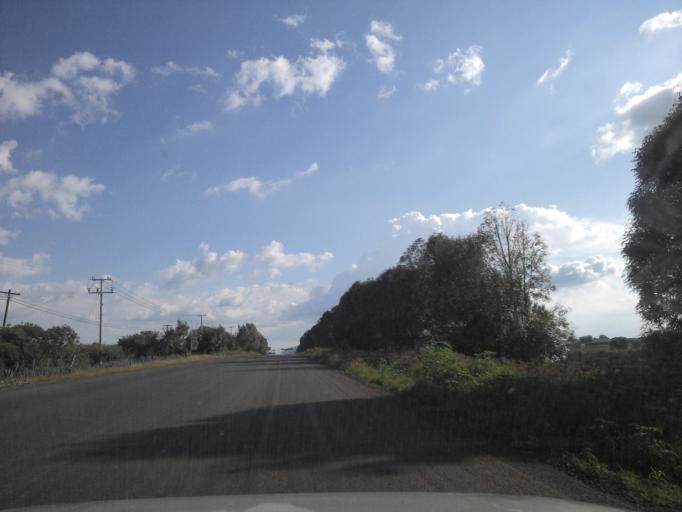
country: MX
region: Jalisco
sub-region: Atotonilco el Alto
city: Ojo de Agua de Moran
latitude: 20.5886
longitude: -102.4964
